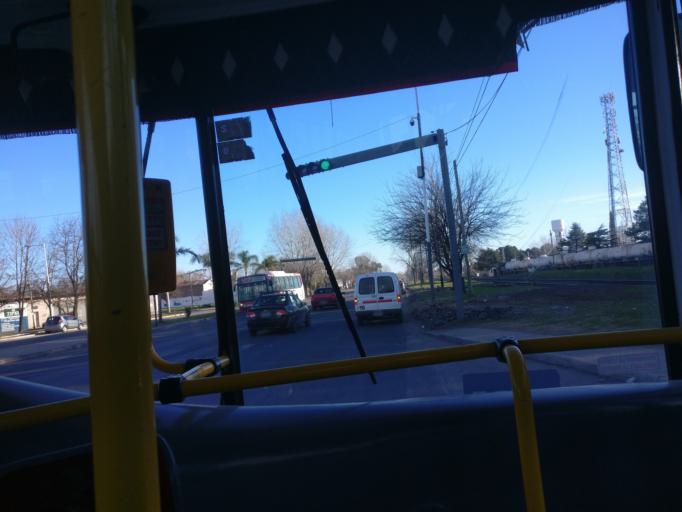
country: AR
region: Buenos Aires
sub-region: Partido de Ezeiza
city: Ezeiza
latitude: -34.9010
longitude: -58.5826
